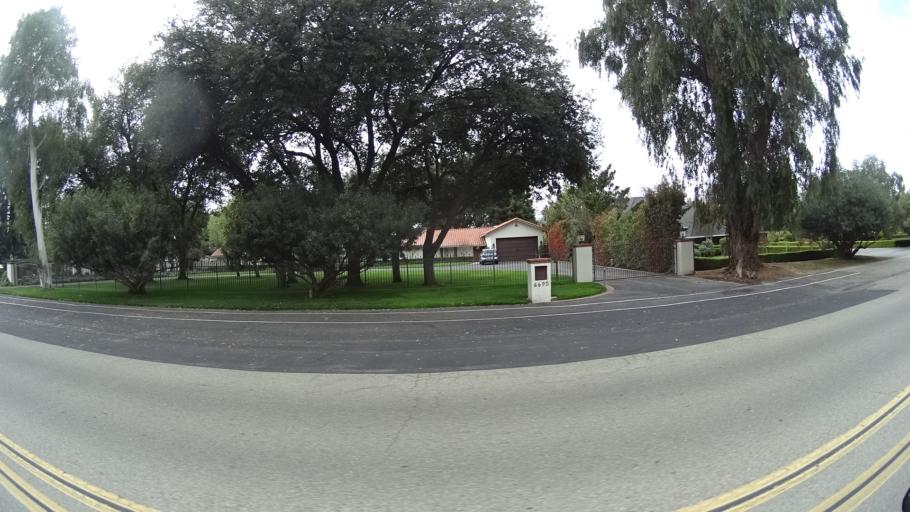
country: US
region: California
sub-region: Fresno County
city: Fresno
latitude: 36.8353
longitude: -119.8354
